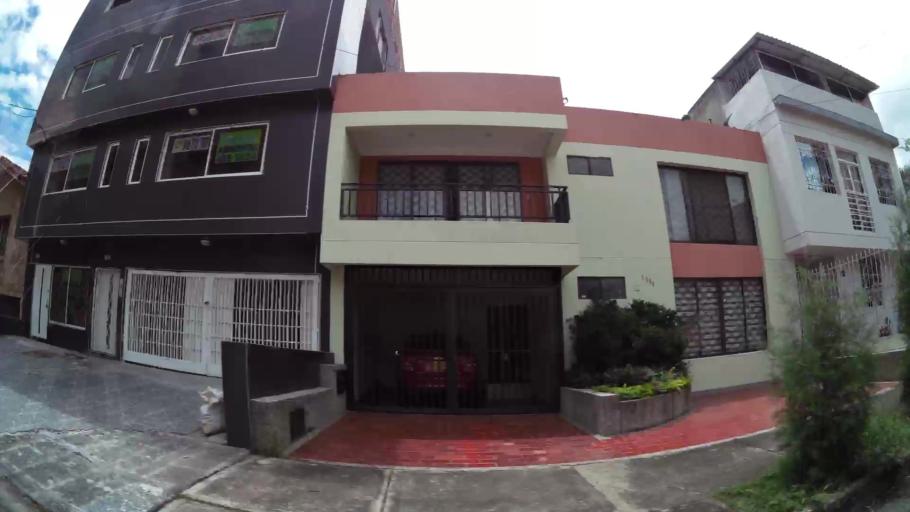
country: CO
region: Valle del Cauca
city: Cali
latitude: 3.3852
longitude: -76.5295
